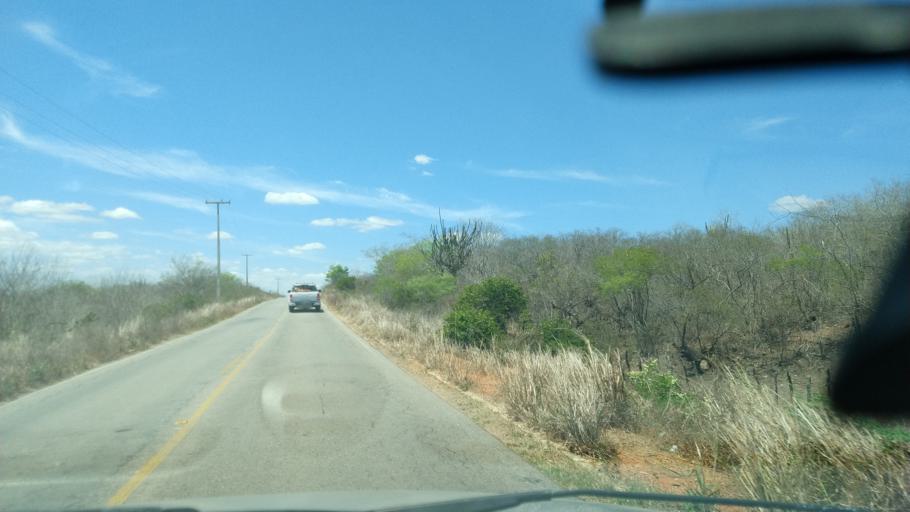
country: BR
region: Rio Grande do Norte
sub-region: Sao Paulo Do Potengi
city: Sao Paulo do Potengi
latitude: -5.9051
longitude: -35.6086
